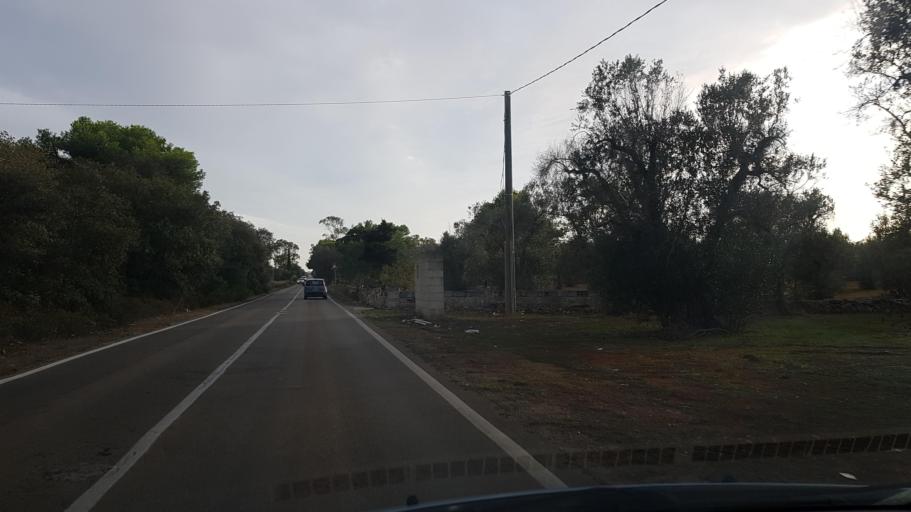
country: IT
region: Apulia
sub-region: Provincia di Brindisi
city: Torchiarolo
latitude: 40.4823
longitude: 18.1262
